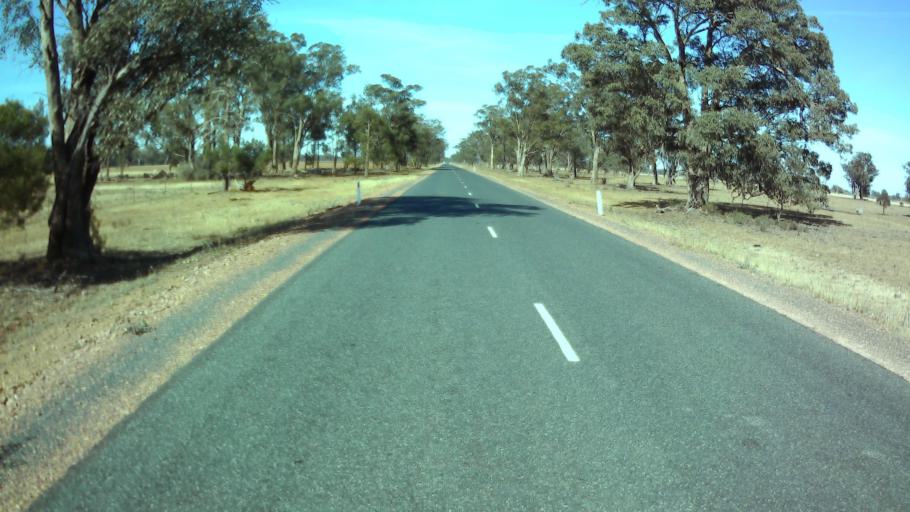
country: AU
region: New South Wales
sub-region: Weddin
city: Grenfell
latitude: -34.1010
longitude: 147.8755
